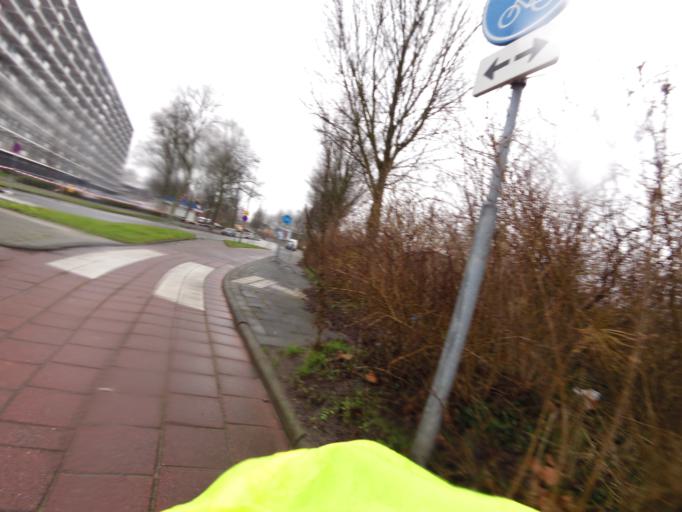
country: NL
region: South Holland
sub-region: Gemeente Maassluis
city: Maassluis
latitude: 51.9392
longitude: 4.2327
